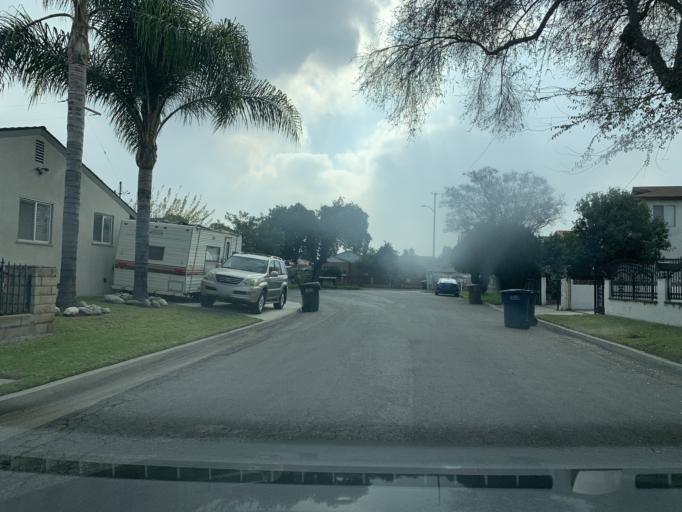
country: US
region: California
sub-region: Los Angeles County
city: South El Monte
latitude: 34.0604
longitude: -118.0488
